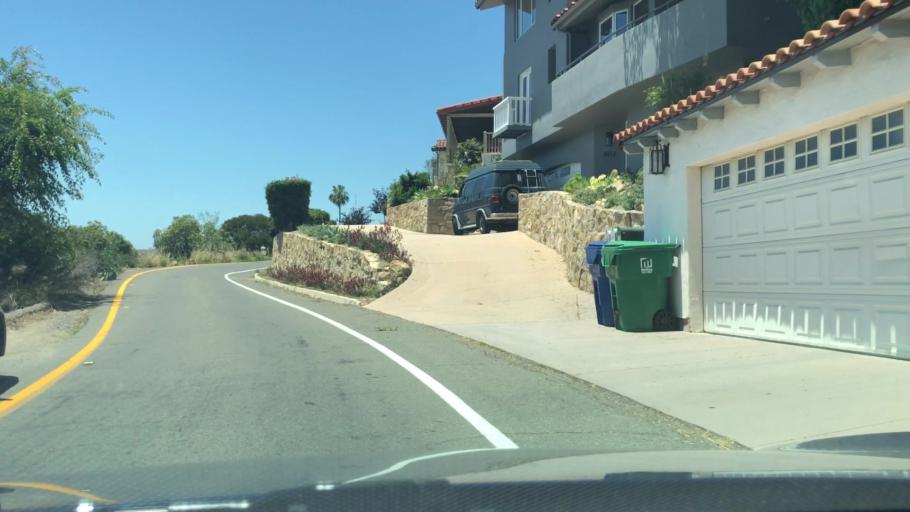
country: US
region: California
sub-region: Santa Barbara County
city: Santa Barbara
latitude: 34.4361
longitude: -119.6883
